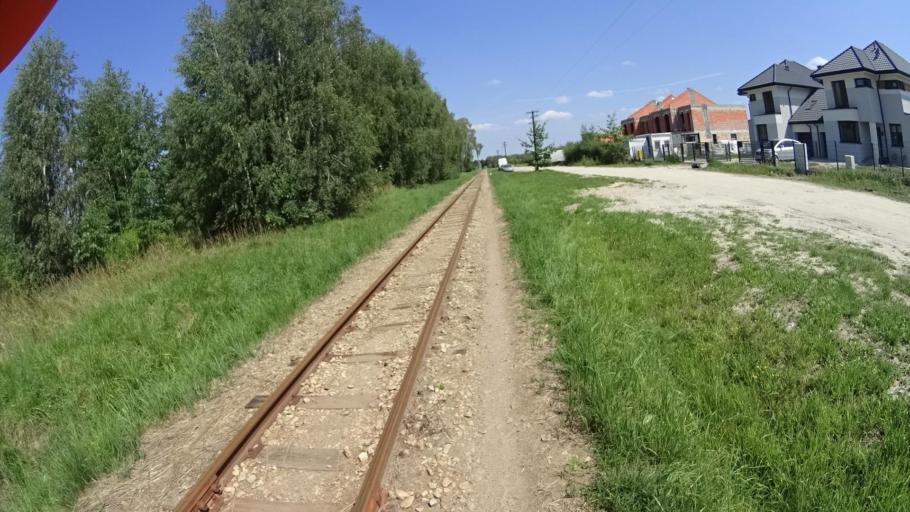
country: PL
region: Masovian Voivodeship
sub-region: Powiat piaseczynski
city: Lesznowola
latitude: 52.0230
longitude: 20.9407
